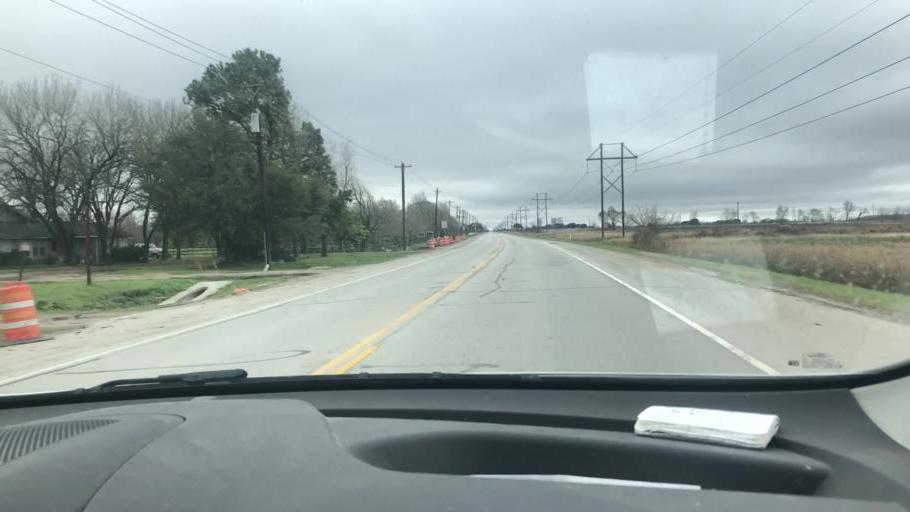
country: US
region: Texas
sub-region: Wharton County
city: Boling
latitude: 29.2117
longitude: -96.0267
